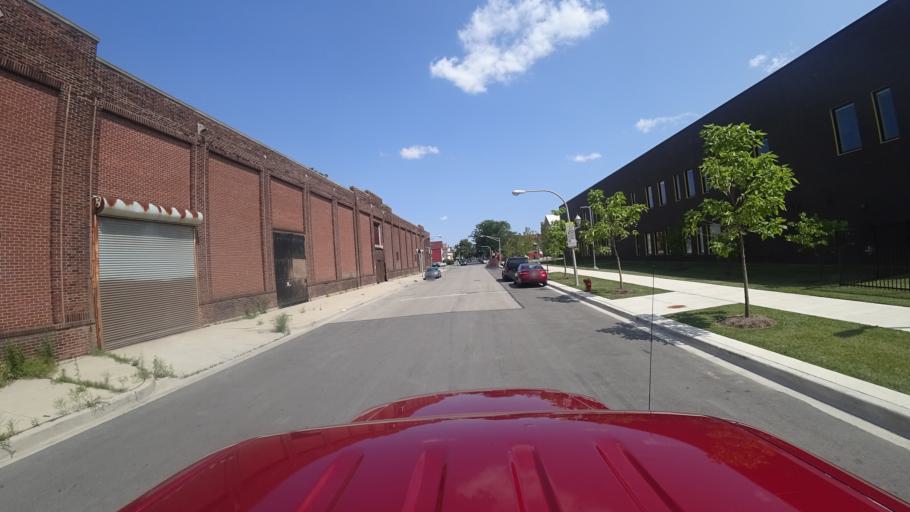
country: US
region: Illinois
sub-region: Cook County
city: Chicago
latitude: 41.8073
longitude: -87.6978
